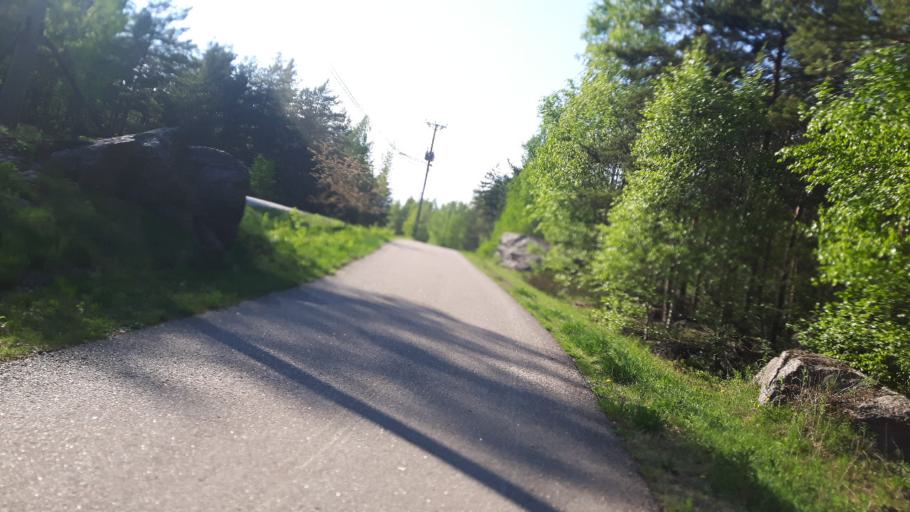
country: FI
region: Kymenlaakso
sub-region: Kotka-Hamina
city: Kotka
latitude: 60.4378
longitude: 26.8718
